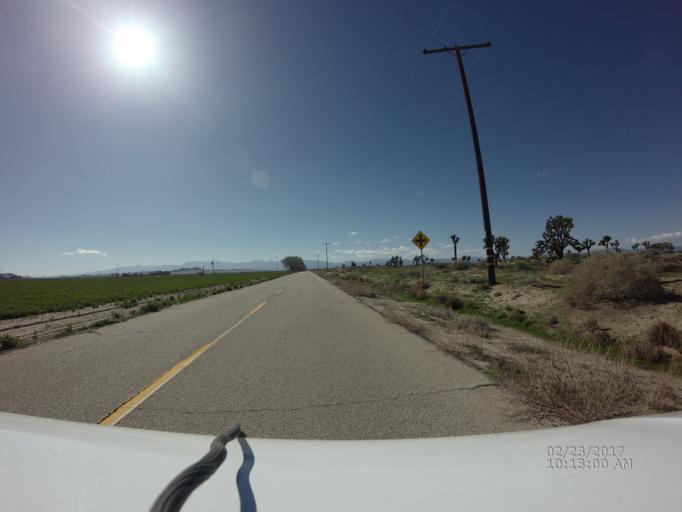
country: US
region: California
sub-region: Los Angeles County
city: Lake Los Angeles
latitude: 34.7066
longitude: -117.9342
